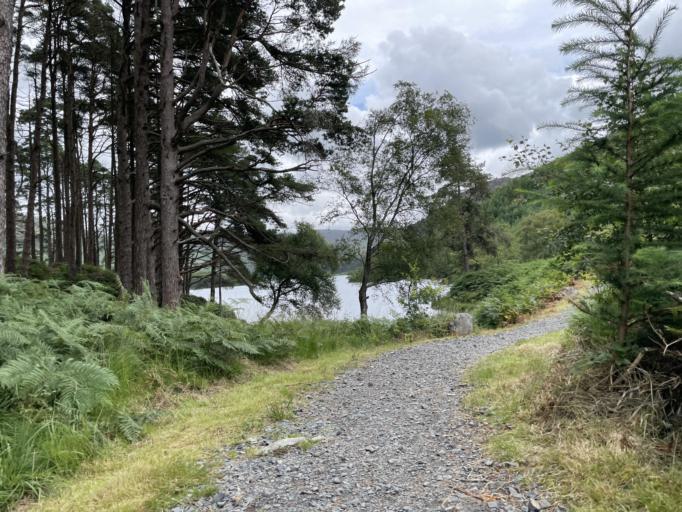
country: GB
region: Scotland
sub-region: Dumfries and Galloway
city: Newton Stewart
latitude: 55.0873
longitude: -4.4936
